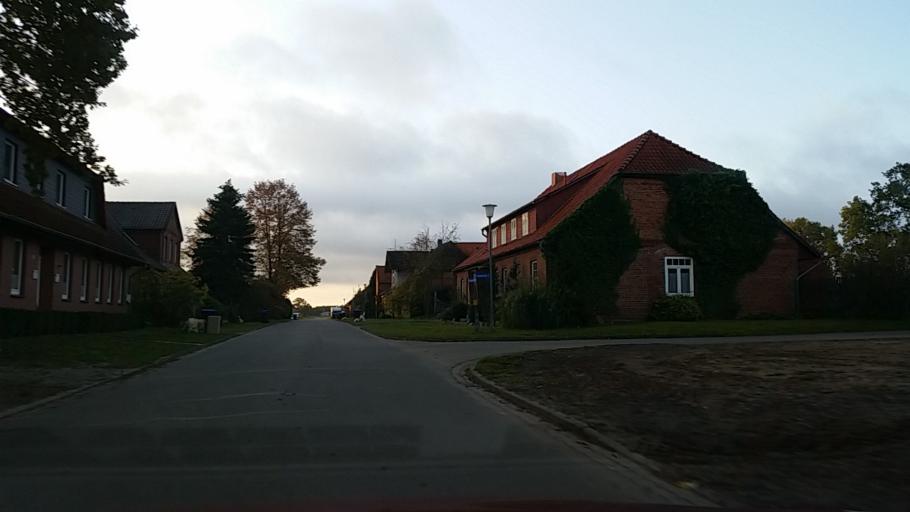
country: DE
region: Lower Saxony
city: Luder
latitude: 52.8106
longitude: 10.6708
